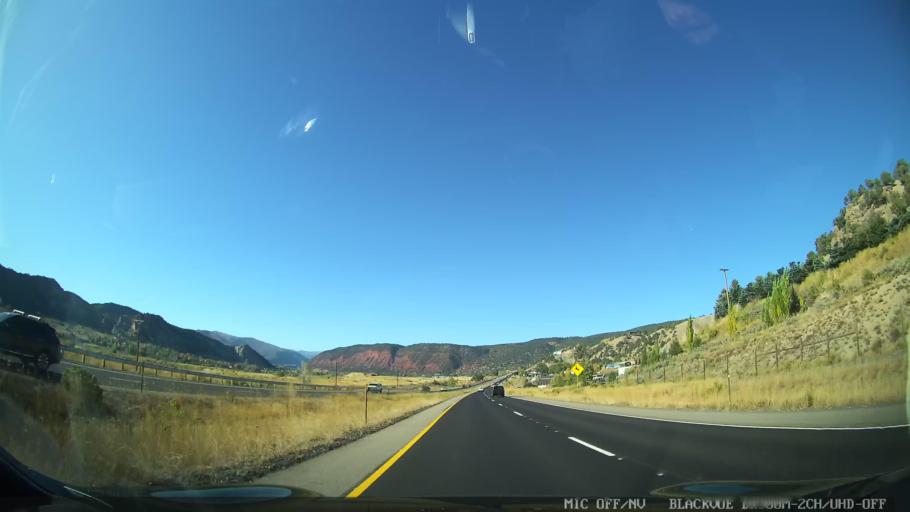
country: US
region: Colorado
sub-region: Garfield County
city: Carbondale
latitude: 39.4490
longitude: -107.2617
